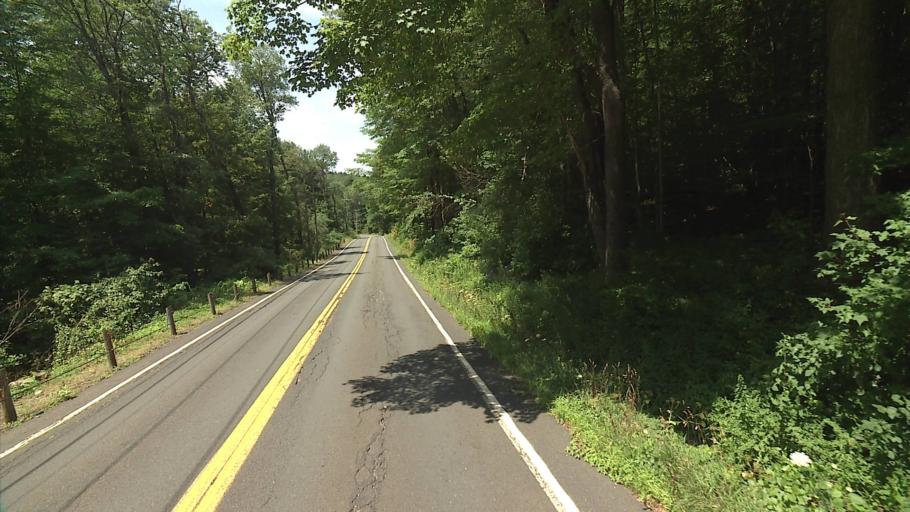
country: US
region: Connecticut
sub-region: Litchfield County
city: Winchester Center
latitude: 41.9896
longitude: -73.1488
